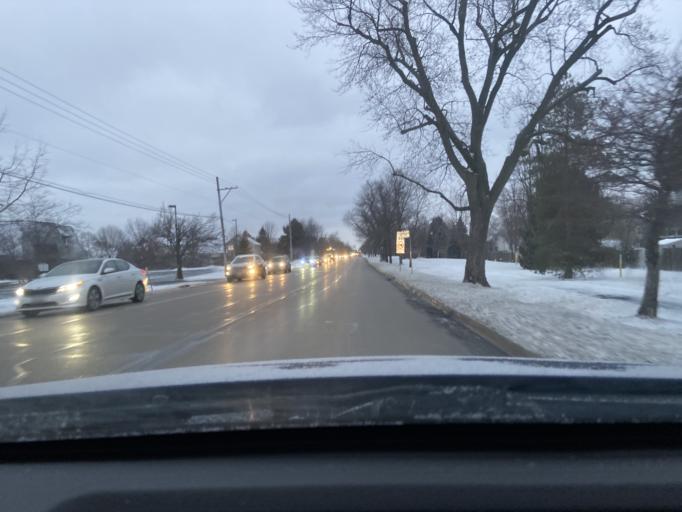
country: US
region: Illinois
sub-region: Lake County
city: Grayslake
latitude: 42.3450
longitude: -88.0240
